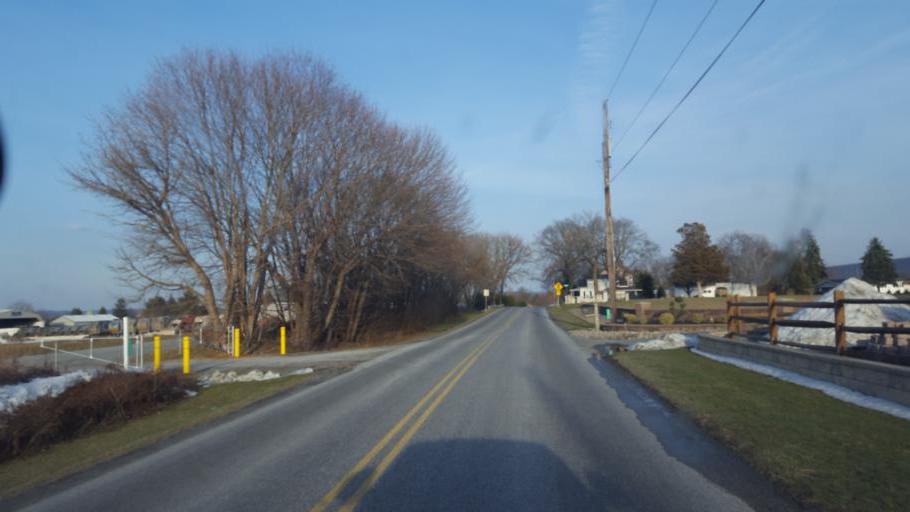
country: US
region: Pennsylvania
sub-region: Lancaster County
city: East Earl
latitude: 40.1097
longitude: -76.0364
